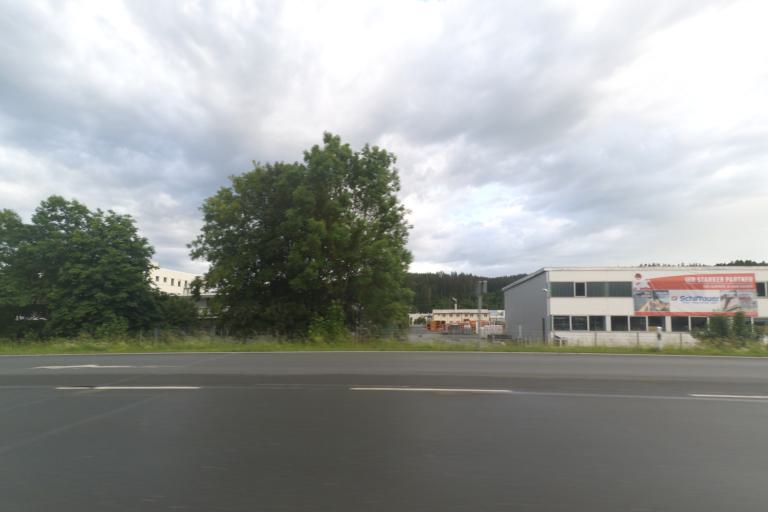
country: DE
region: Bavaria
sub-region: Upper Franconia
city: Kronach
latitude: 50.2332
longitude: 11.3445
